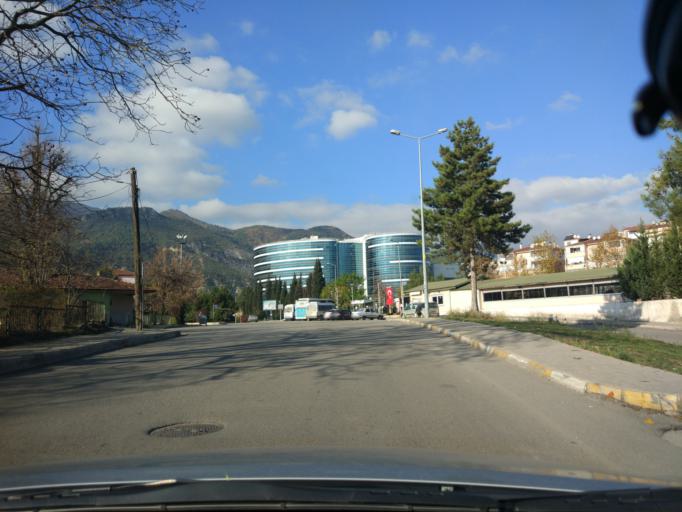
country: TR
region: Karabuk
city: Karabuk
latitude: 41.2061
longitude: 32.6201
